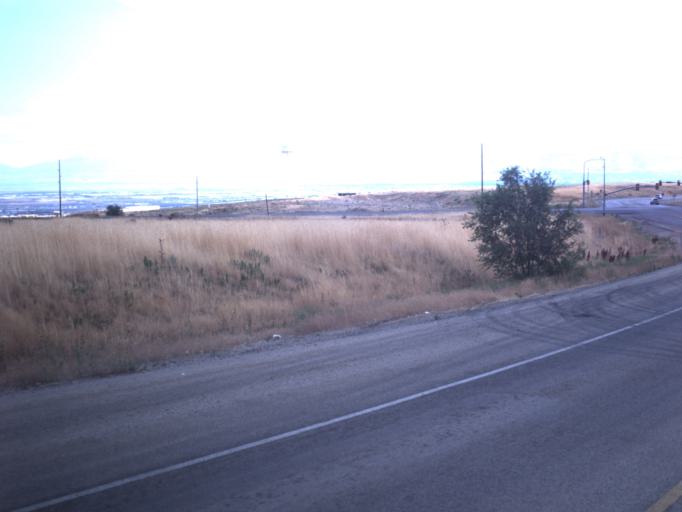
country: US
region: Utah
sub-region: Salt Lake County
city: Oquirrh
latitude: 40.6530
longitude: -112.0783
